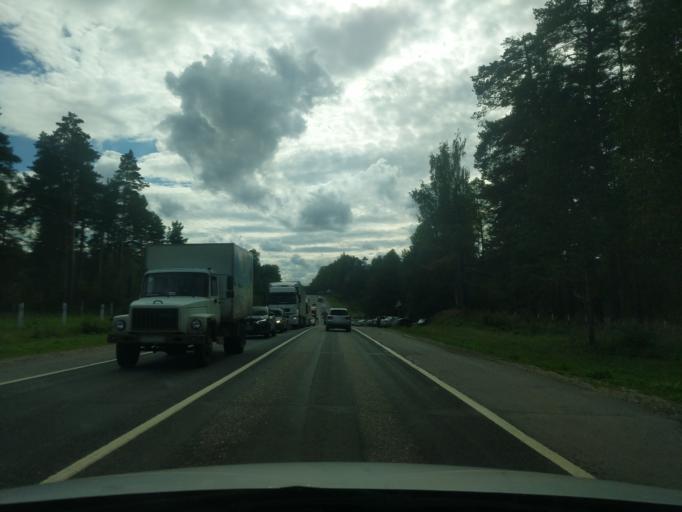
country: RU
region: Jaroslavl
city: Levashevo
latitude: 57.6730
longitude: 40.5836
